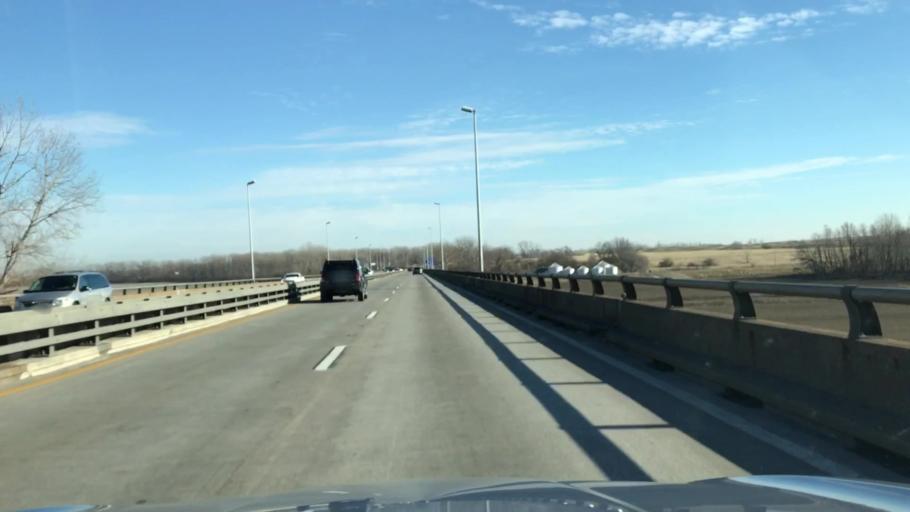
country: US
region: Missouri
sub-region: Saint Louis County
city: Glasgow Village
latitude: 38.7630
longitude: -90.1667
